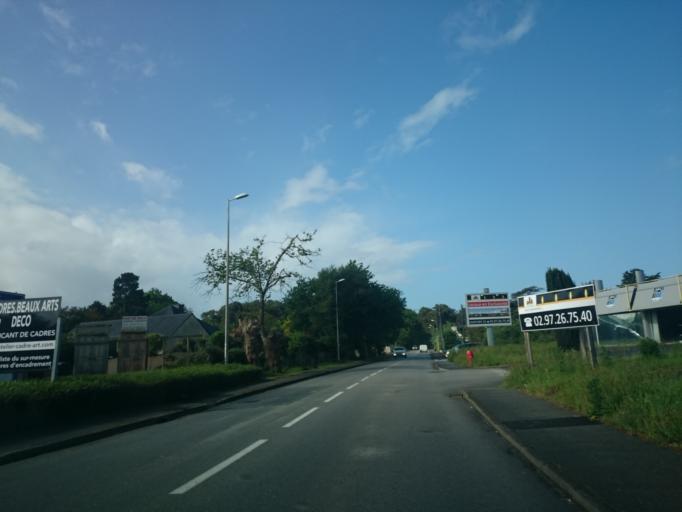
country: FR
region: Brittany
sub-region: Departement du Morbihan
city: Arradon
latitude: 47.6540
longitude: -2.7936
